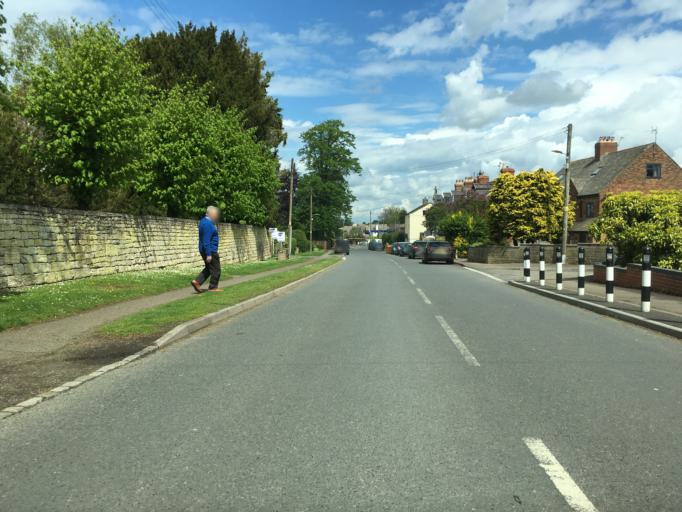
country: GB
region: England
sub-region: Gloucestershire
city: Stonehouse
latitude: 51.7311
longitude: -2.2742
